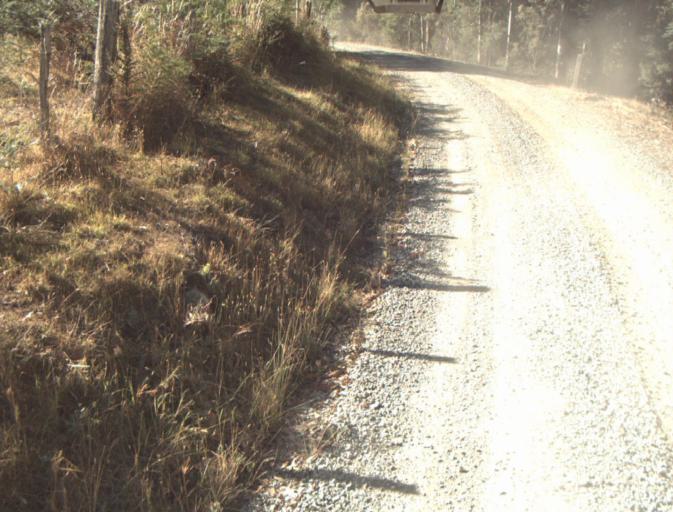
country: AU
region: Tasmania
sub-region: Launceston
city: Mayfield
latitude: -41.2891
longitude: 147.1971
